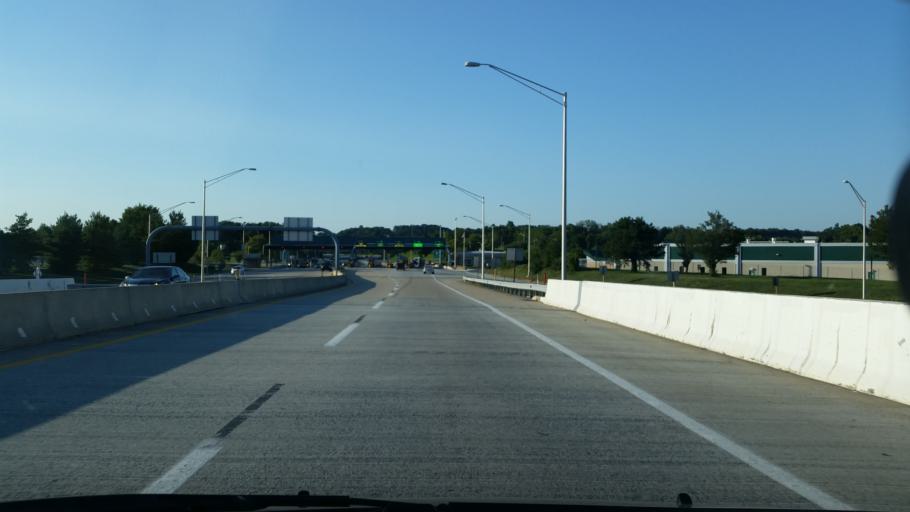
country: US
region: Pennsylvania
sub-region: Dauphin County
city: Highspire
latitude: 40.2147
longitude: -76.7862
